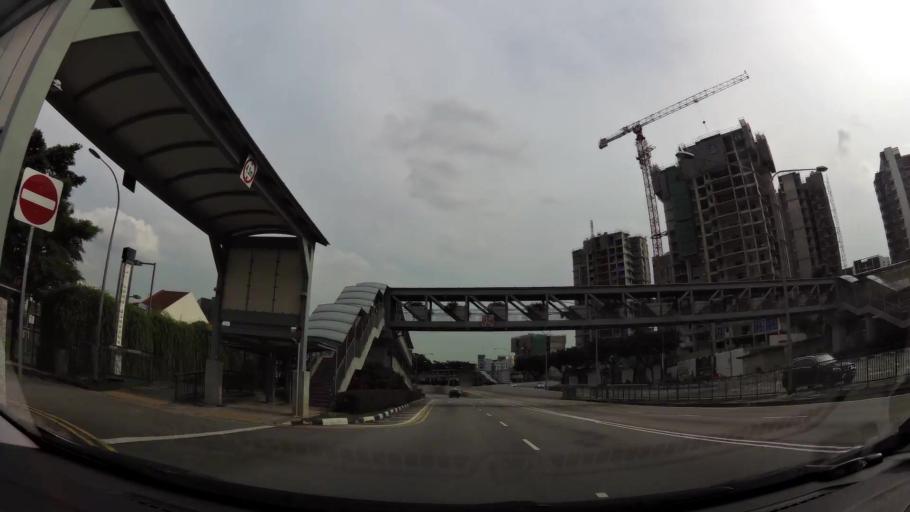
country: SG
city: Singapore
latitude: 1.3438
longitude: 103.8828
